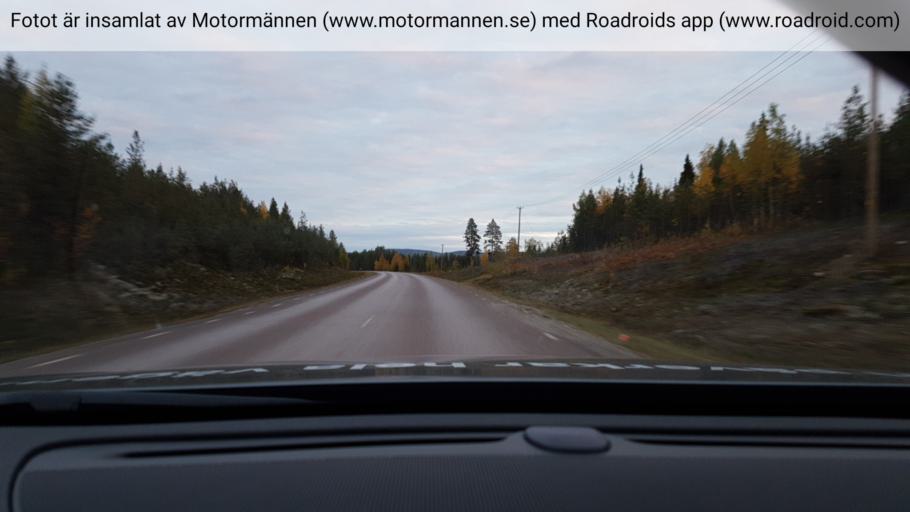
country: SE
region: Norrbotten
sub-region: Alvsbyns Kommun
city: AElvsbyn
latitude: 65.8981
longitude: 20.3371
